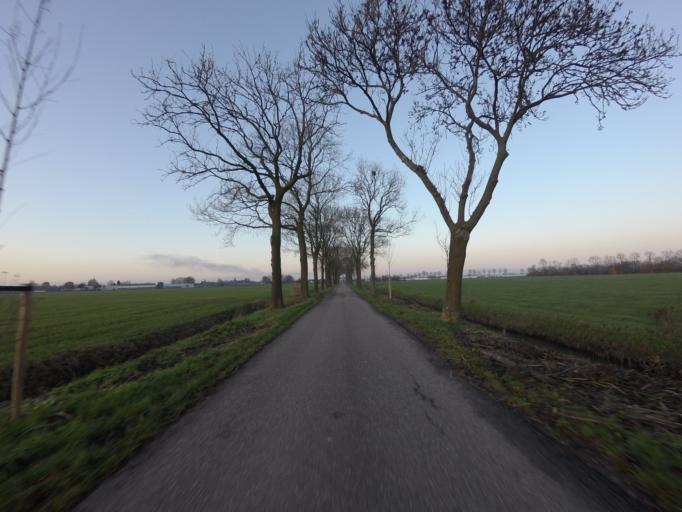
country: NL
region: Gelderland
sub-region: Gemeente Maasdriel
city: Hedel
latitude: 51.7673
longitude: 5.2252
